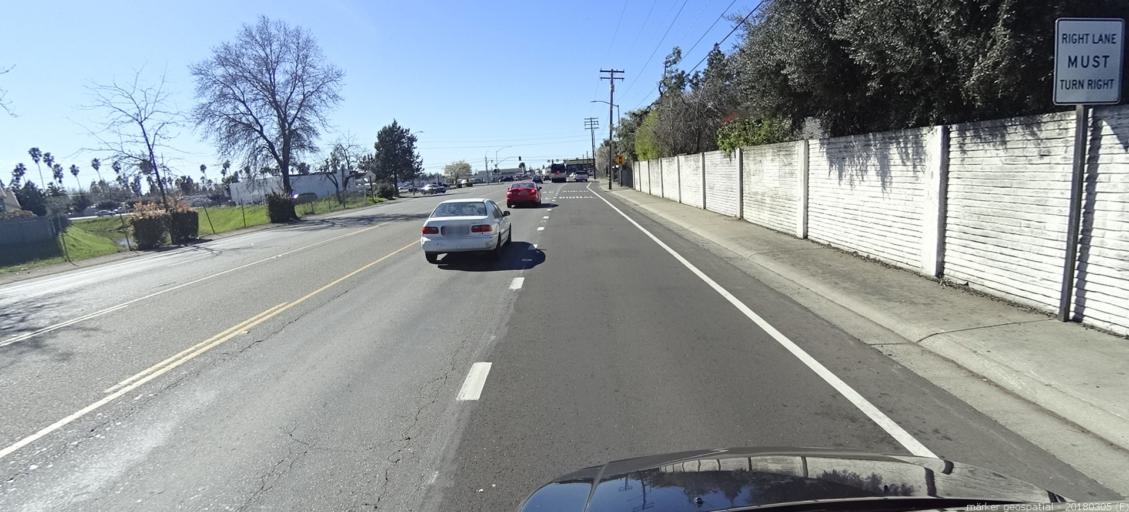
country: US
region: California
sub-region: Sacramento County
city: Florin
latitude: 38.4817
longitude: -121.4202
